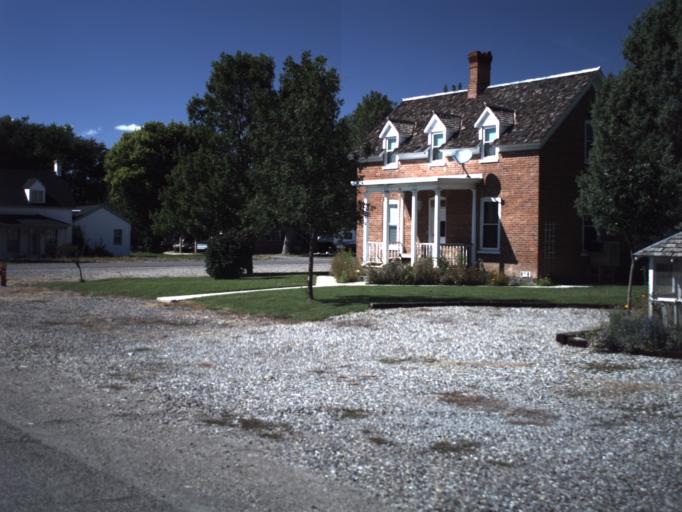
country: US
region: Utah
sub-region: Beaver County
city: Beaver
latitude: 38.2769
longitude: -112.6424
